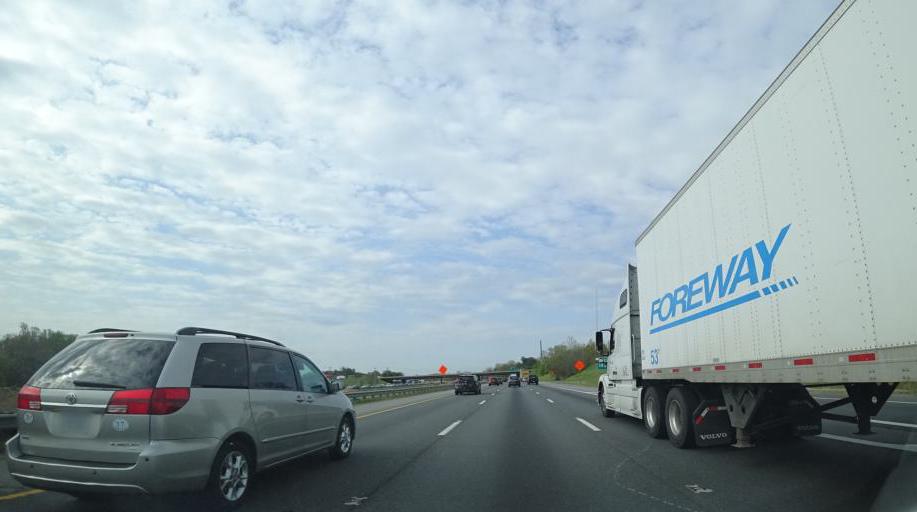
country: US
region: Virginia
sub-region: Stafford County
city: Aquia Harbour
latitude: 38.4686
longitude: -77.4060
